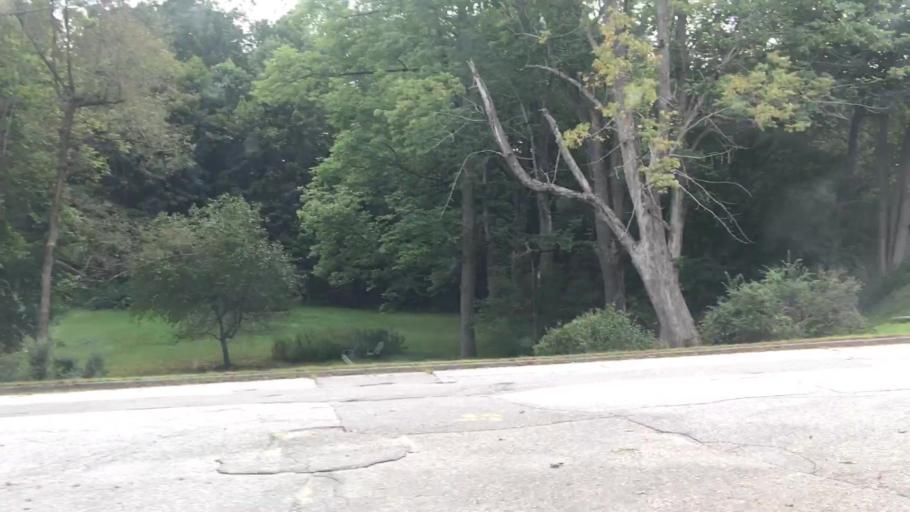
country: US
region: Maine
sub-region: Kennebec County
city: Hallowell
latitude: 44.2857
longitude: -69.7959
